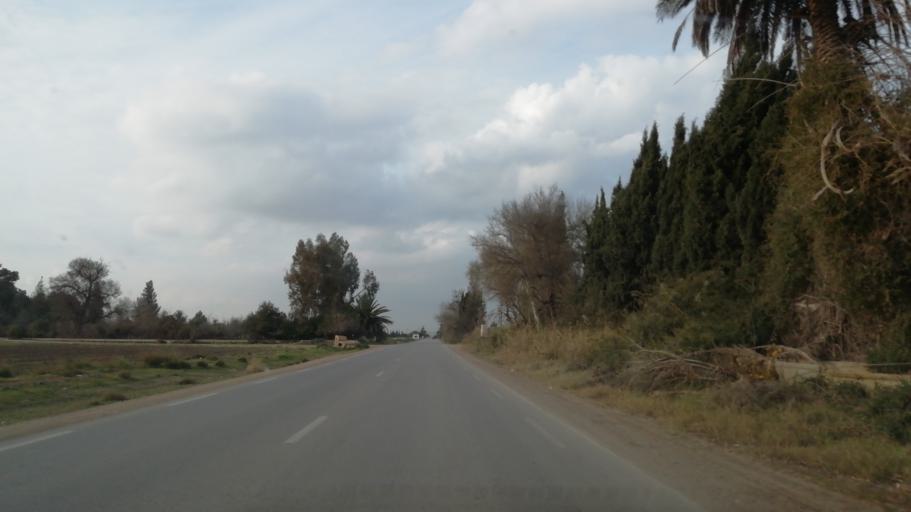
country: DZ
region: Mascara
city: Sig
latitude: 35.6815
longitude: -0.0110
